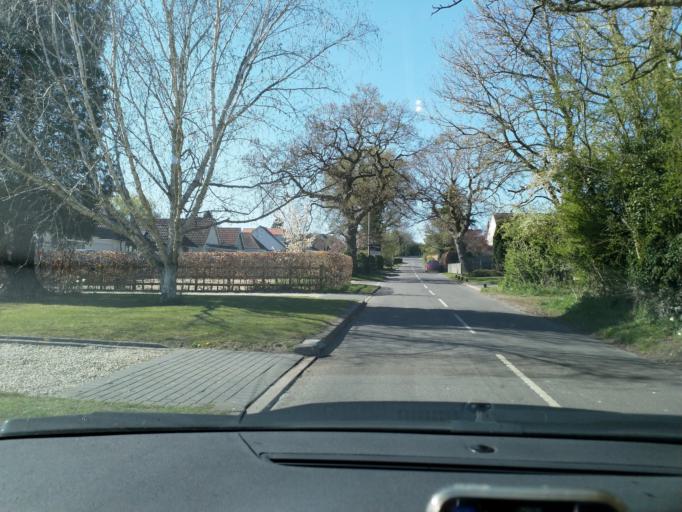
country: GB
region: England
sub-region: Warwickshire
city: Wroxall
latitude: 52.2928
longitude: -1.6721
